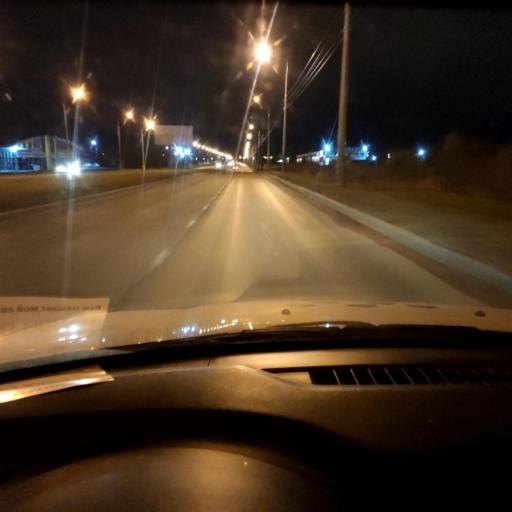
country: RU
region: Samara
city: Tol'yatti
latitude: 53.5574
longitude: 49.3311
